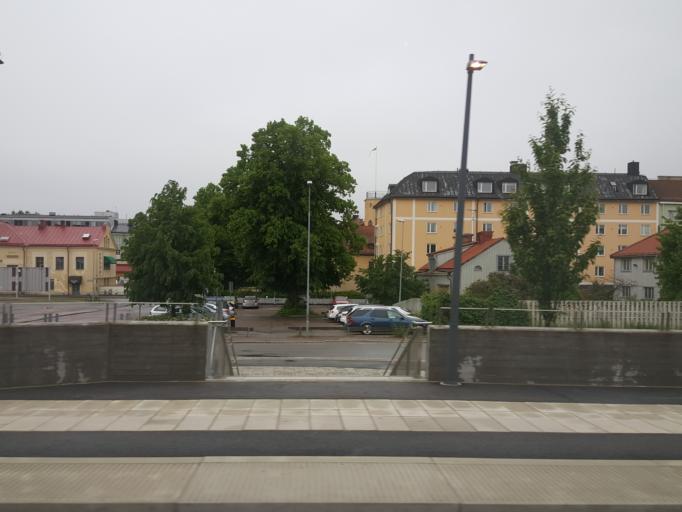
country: SE
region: Uppsala
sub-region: Uppsala Kommun
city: Uppsala
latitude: 59.8562
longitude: 17.6511
